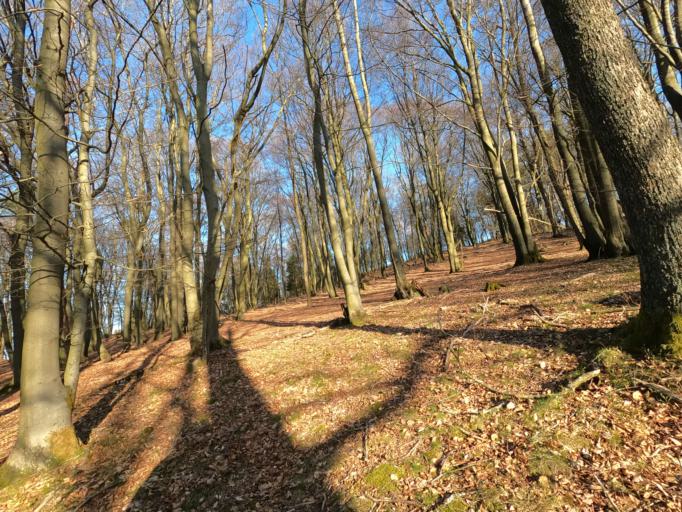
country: DE
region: North Rhine-Westphalia
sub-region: Regierungsbezirk Arnsberg
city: Herscheid
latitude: 51.1666
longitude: 7.7272
